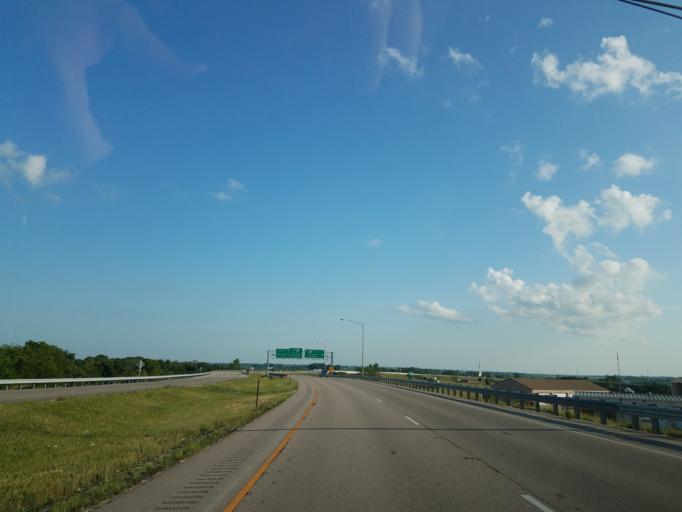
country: US
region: Illinois
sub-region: McLean County
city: Bloomington
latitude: 40.4477
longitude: -89.0162
